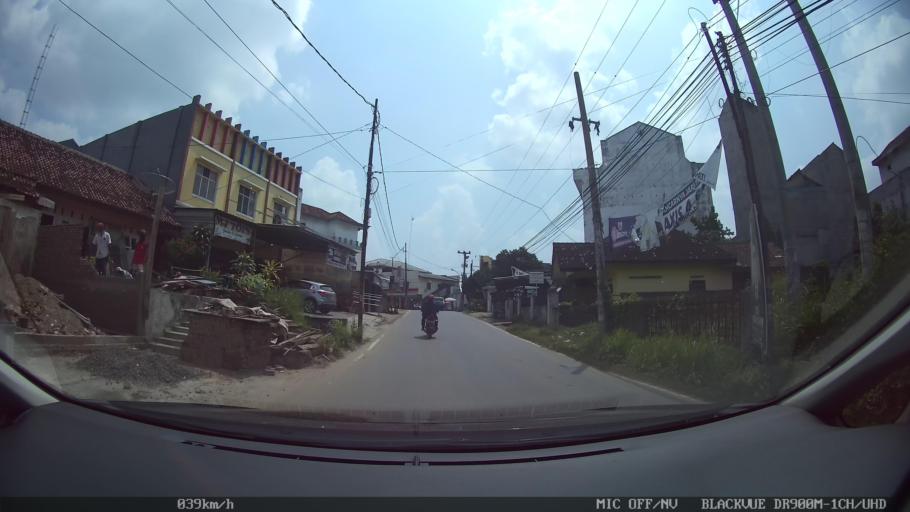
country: ID
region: Lampung
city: Pringsewu
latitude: -5.3620
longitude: 104.9766
